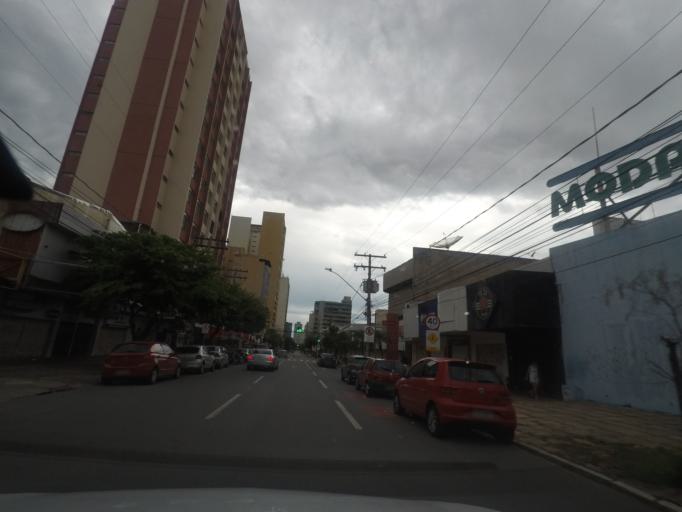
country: BR
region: Goias
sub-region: Goiania
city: Goiania
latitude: -16.6767
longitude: -49.2601
